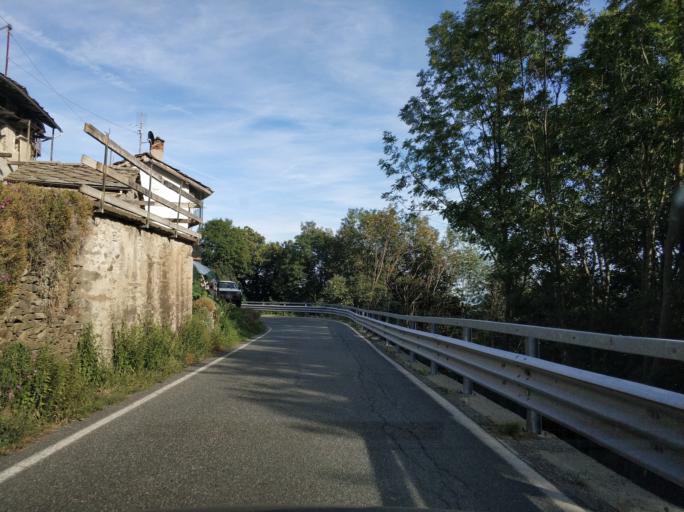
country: IT
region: Piedmont
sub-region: Provincia di Torino
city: Monastero di Lanzo
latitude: 45.3047
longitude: 7.4355
